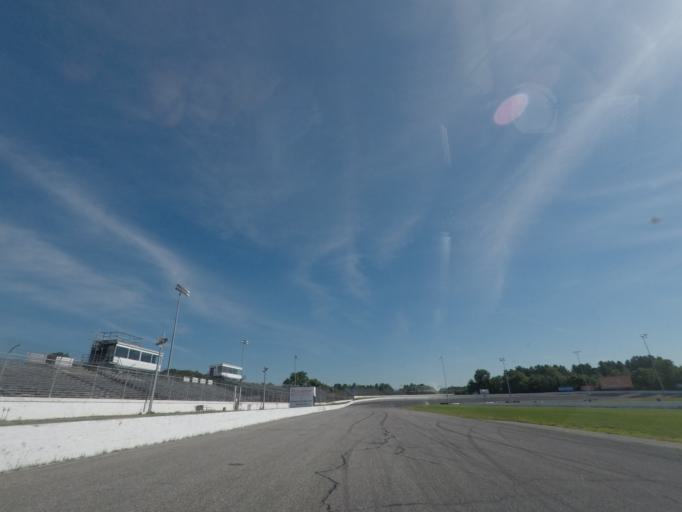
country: US
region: Connecticut
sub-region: Windham County
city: Thompson
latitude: 41.9814
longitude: -71.8256
